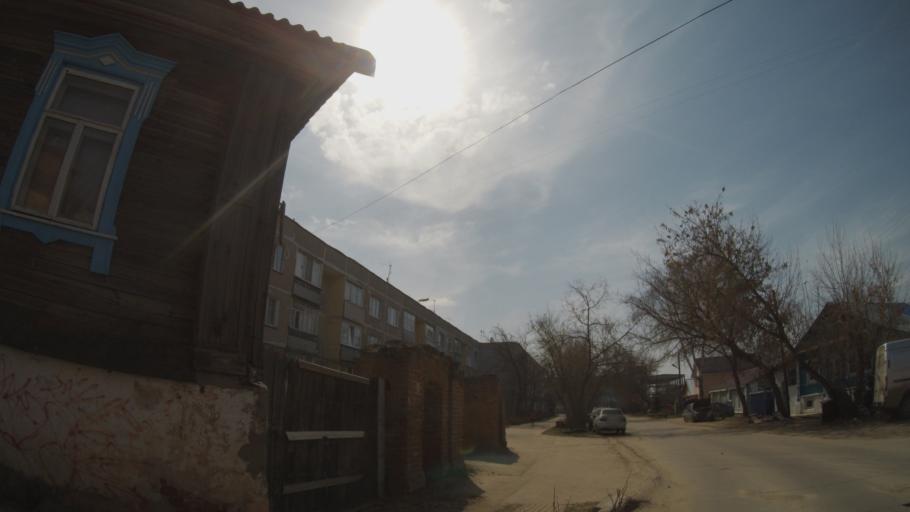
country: RU
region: Nizjnij Novgorod
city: Vyyezdnoye
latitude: 55.3854
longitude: 43.8117
